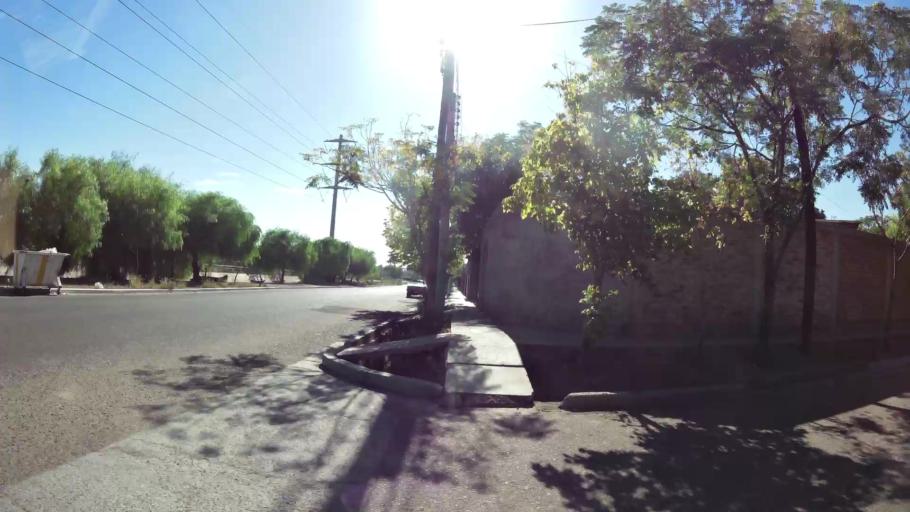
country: AR
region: Mendoza
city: Las Heras
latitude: -32.8723
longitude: -68.8675
